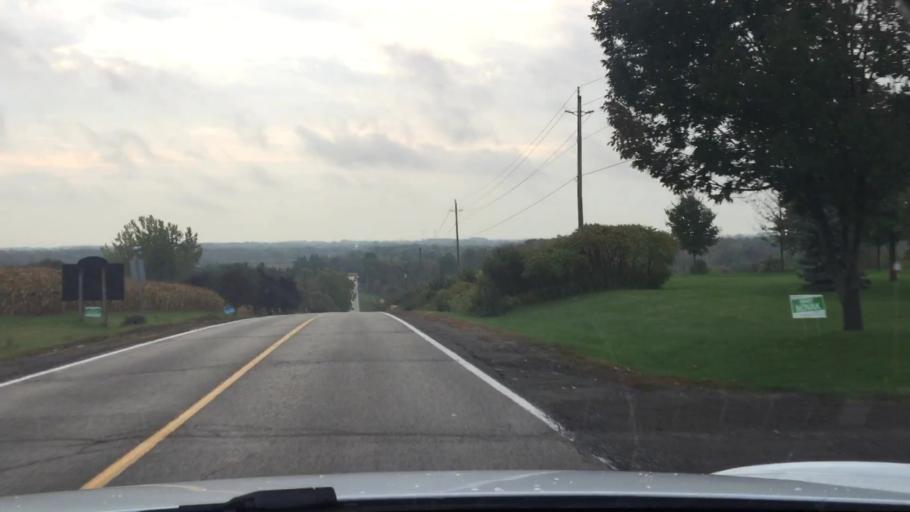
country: CA
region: Ontario
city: Oshawa
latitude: 43.9389
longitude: -78.8008
